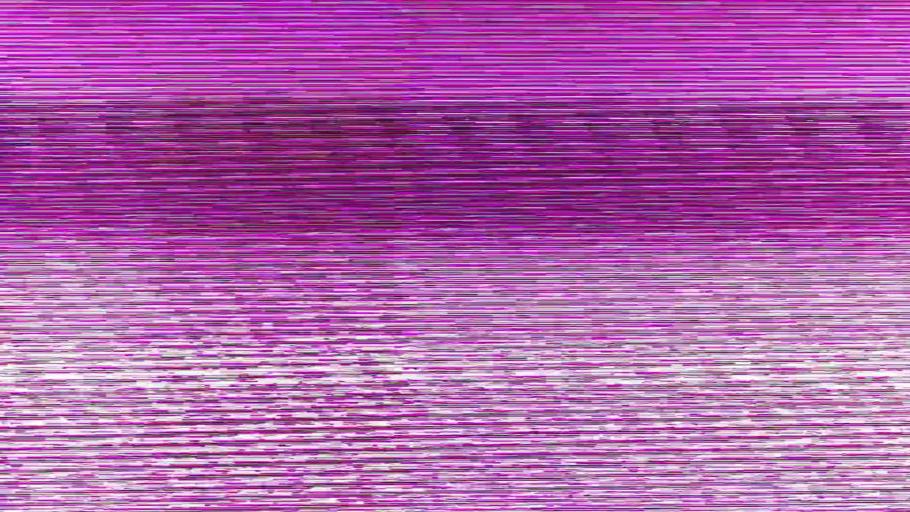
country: US
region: Michigan
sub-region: Oakland County
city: Sylvan Lake
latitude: 42.6279
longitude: -83.3200
